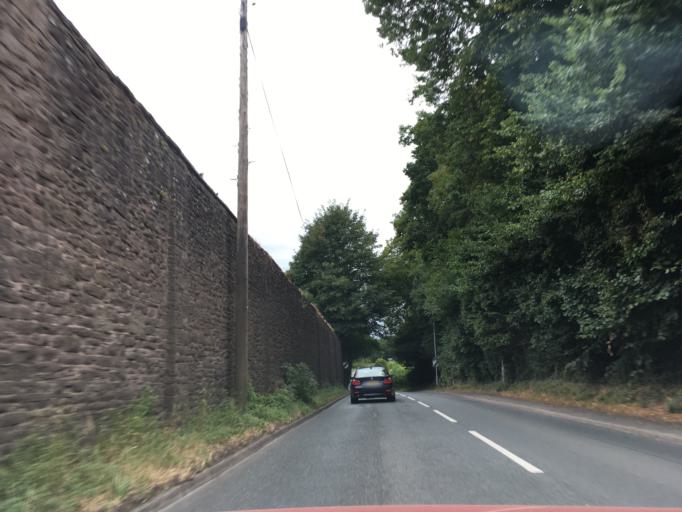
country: GB
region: Wales
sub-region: Monmouthshire
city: Gilwern
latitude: 51.8646
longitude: -3.1427
